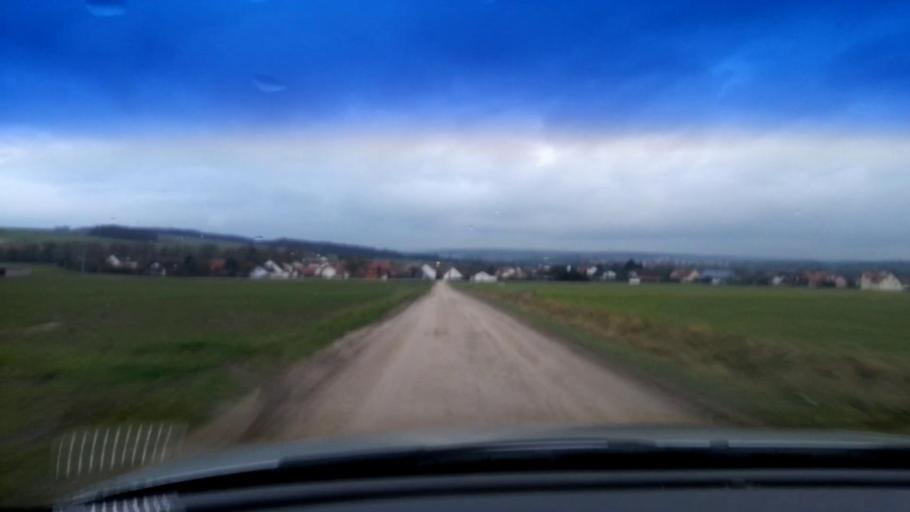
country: DE
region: Bavaria
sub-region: Upper Franconia
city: Litzendorf
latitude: 49.9416
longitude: 11.0033
